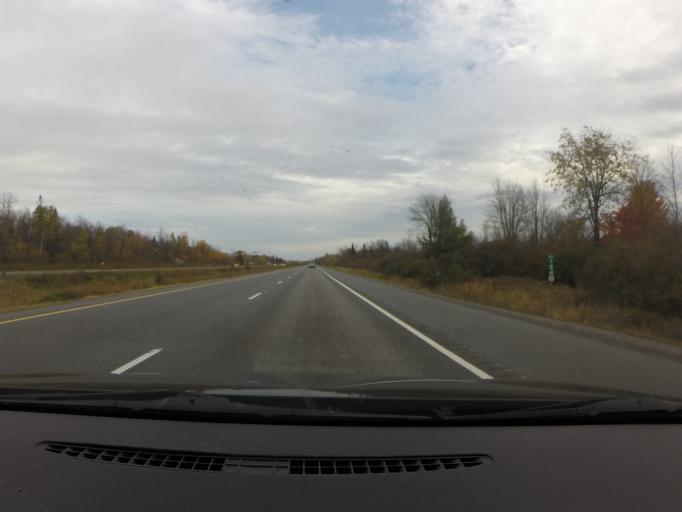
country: CA
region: Ontario
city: Carleton Place
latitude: 45.3071
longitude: -76.0374
